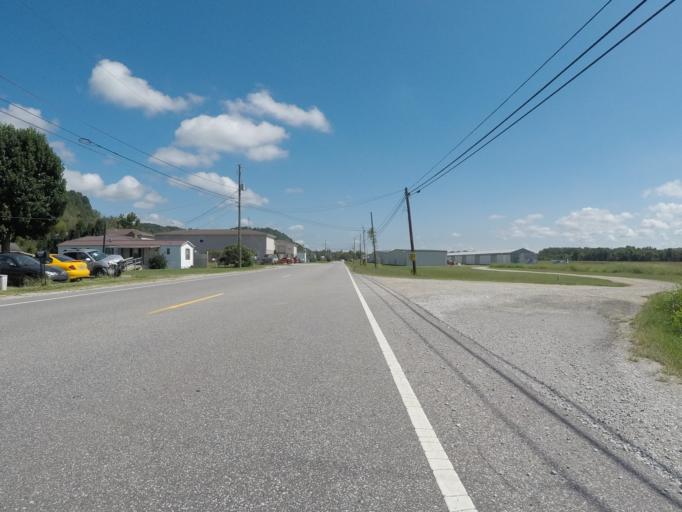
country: US
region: Ohio
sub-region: Lawrence County
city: Burlington
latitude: 38.4202
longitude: -82.4973
